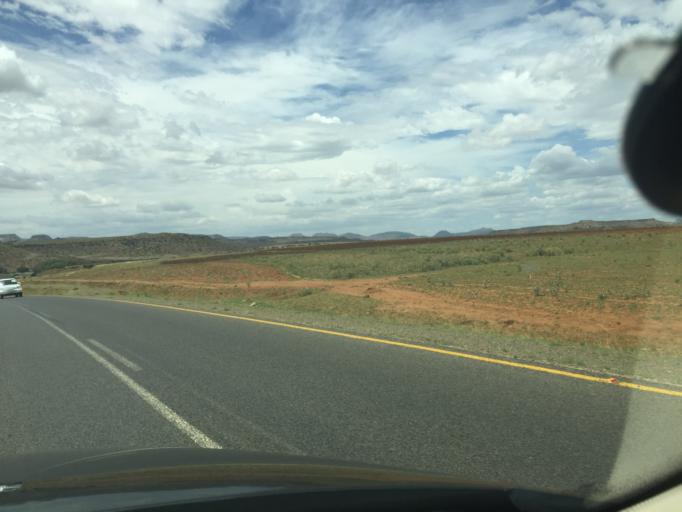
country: LS
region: Mohale's Hoek District
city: Mohale's Hoek
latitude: -30.0866
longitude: 27.4298
